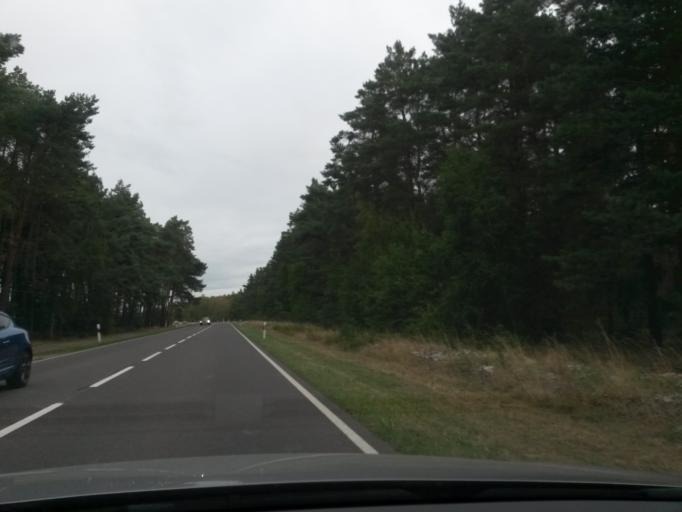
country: DE
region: Saxony-Anhalt
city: Schonhausen
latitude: 52.5576
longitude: 12.0281
